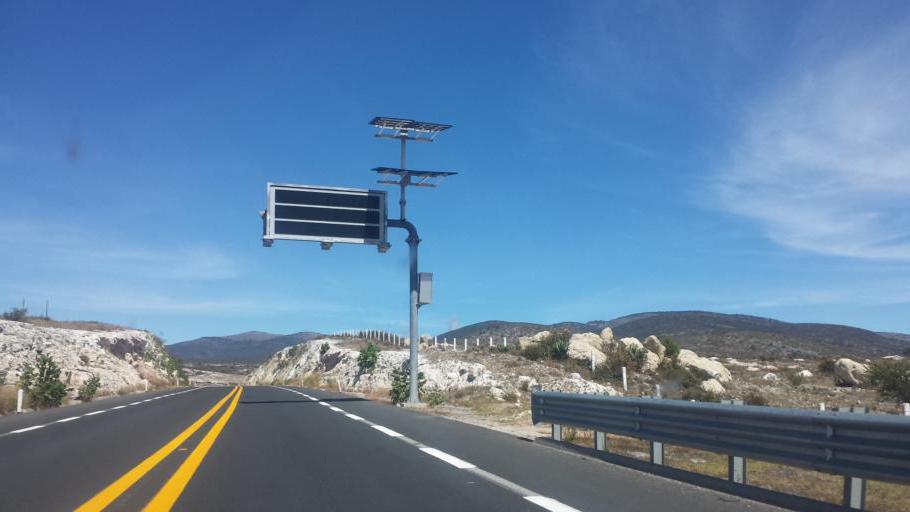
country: MX
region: Oaxaca
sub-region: Villa Tejupam de la Union
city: Villa Tejupam de la Union
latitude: 17.9221
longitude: -97.3596
